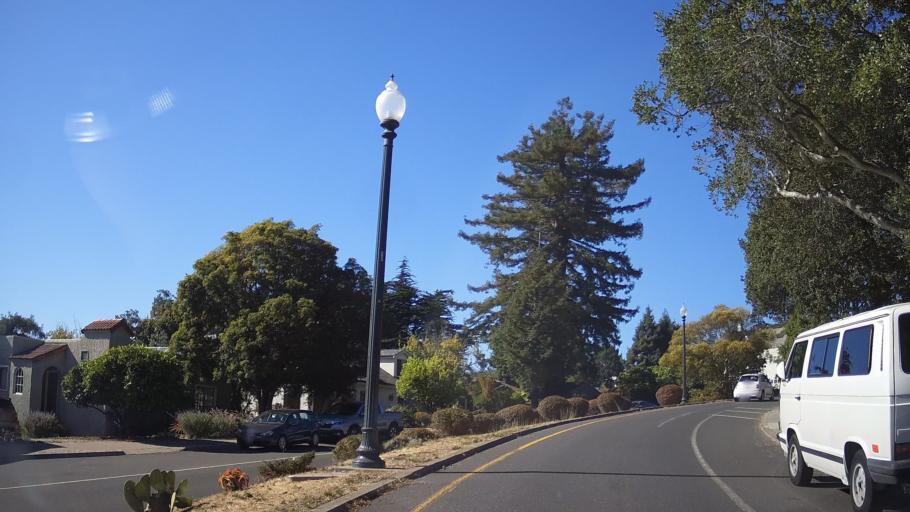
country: US
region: California
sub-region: Contra Costa County
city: Kensington
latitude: 37.8993
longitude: -122.2775
